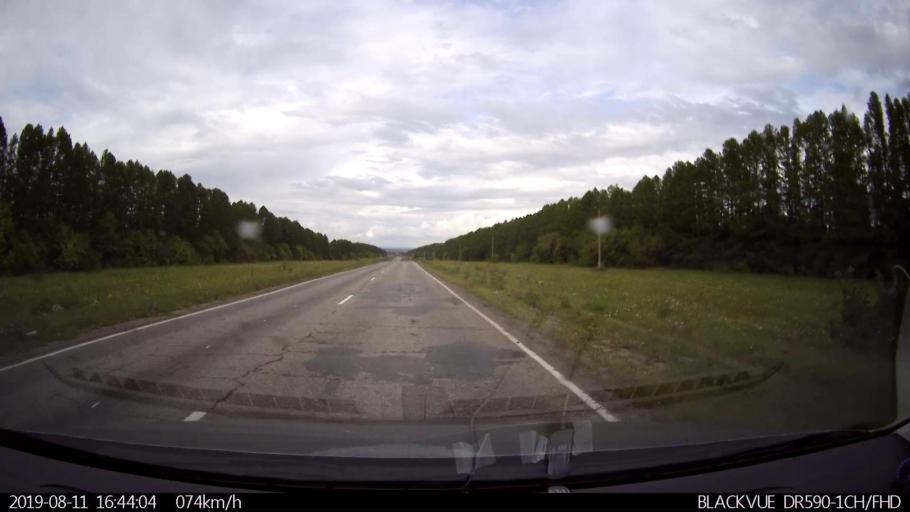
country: RU
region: Ulyanovsk
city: Mayna
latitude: 54.1755
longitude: 47.6778
